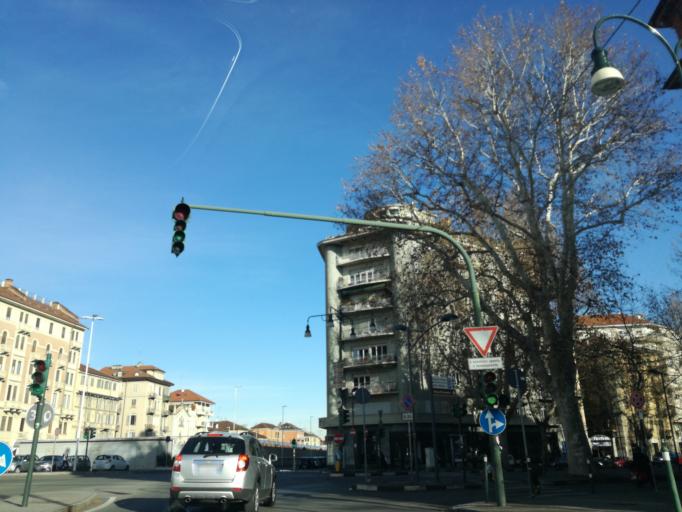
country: IT
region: Piedmont
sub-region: Provincia di Torino
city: Turin
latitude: 45.0773
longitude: 7.6694
